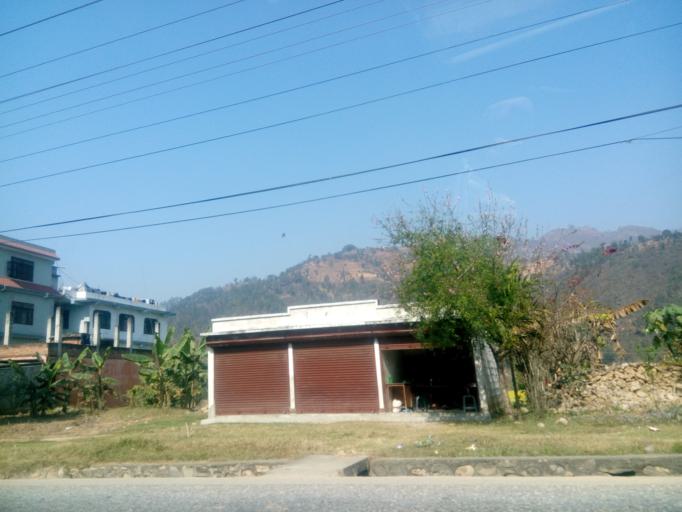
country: NP
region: Central Region
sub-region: Narayani Zone
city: Hitura
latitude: 27.8046
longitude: 84.8763
